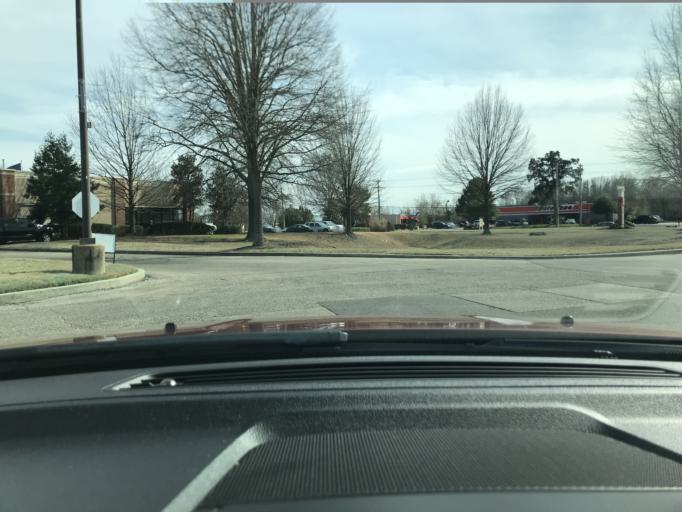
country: US
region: Tennessee
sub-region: Shelby County
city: Collierville
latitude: 35.0473
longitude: -89.6958
